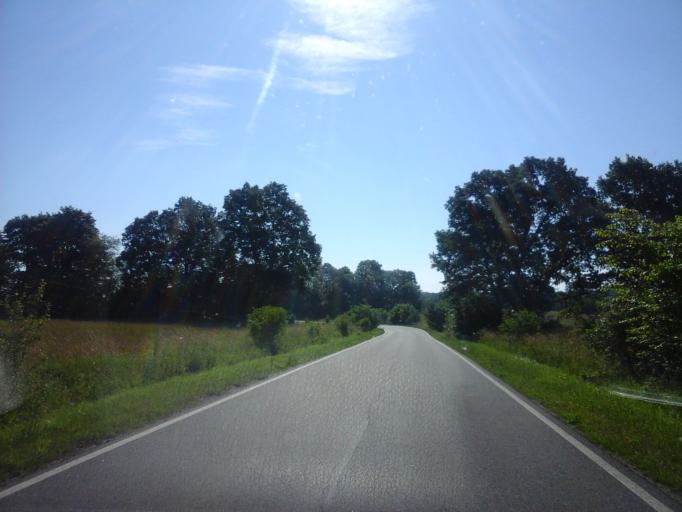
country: PL
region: West Pomeranian Voivodeship
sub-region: Powiat drawski
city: Zlocieniec
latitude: 53.6359
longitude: 15.9494
